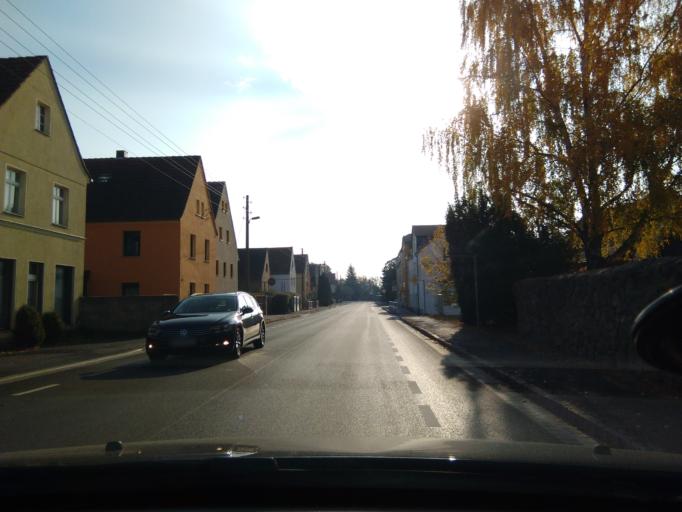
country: DE
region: Saxony
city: Coswig
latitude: 51.1308
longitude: 13.5439
